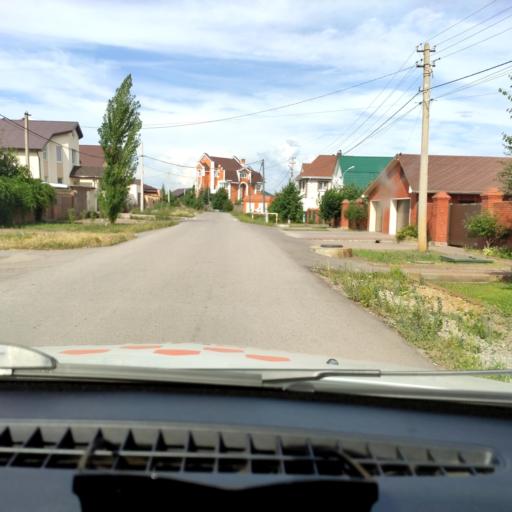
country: RU
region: Bashkortostan
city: Ufa
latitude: 54.6245
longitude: 55.9174
